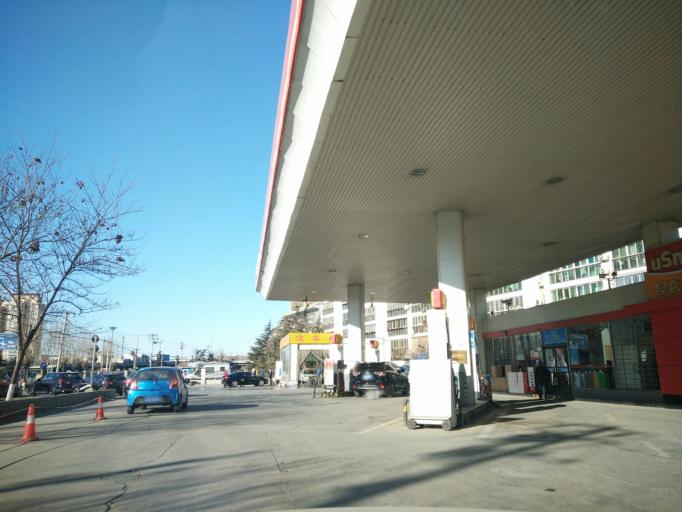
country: CN
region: Beijing
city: Xingfeng
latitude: 39.7210
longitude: 116.3426
